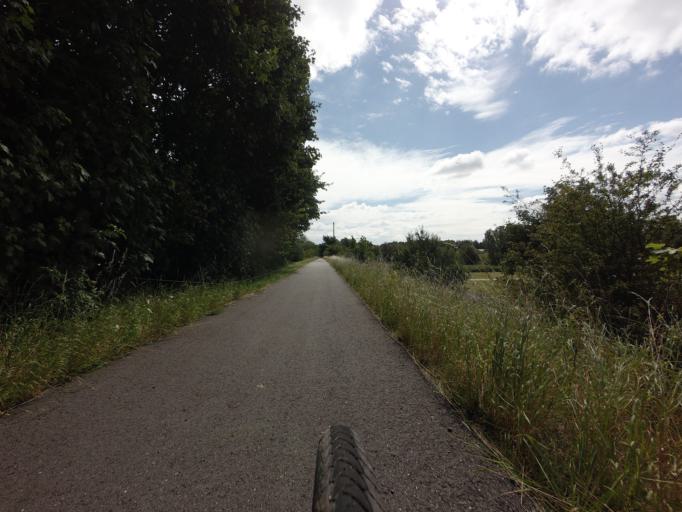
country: DK
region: Central Jutland
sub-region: Norddjurs Kommune
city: Auning
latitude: 56.3931
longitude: 10.4094
